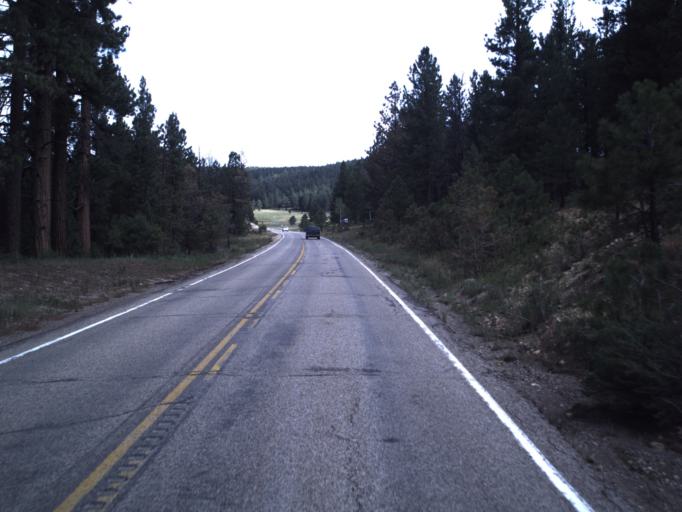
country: US
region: Utah
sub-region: Garfield County
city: Panguitch
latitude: 37.4995
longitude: -112.6221
